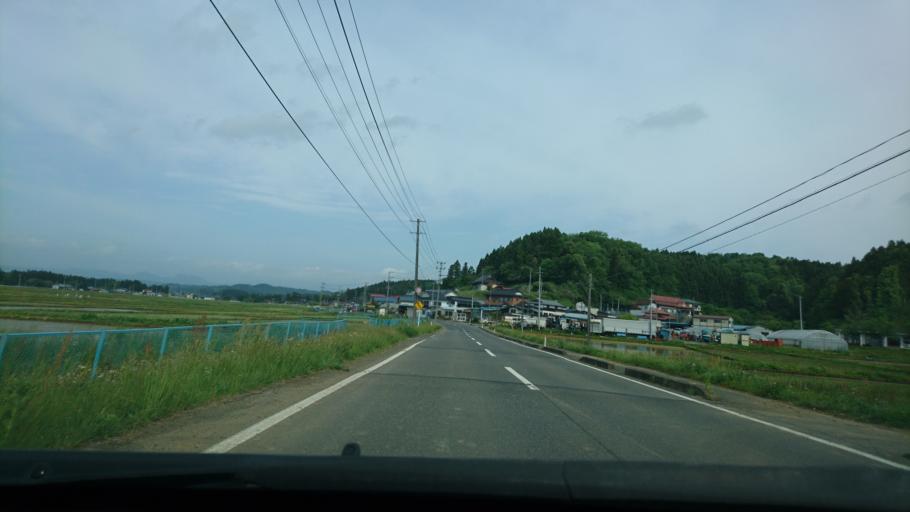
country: JP
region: Iwate
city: Ichinoseki
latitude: 38.8243
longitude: 141.0336
